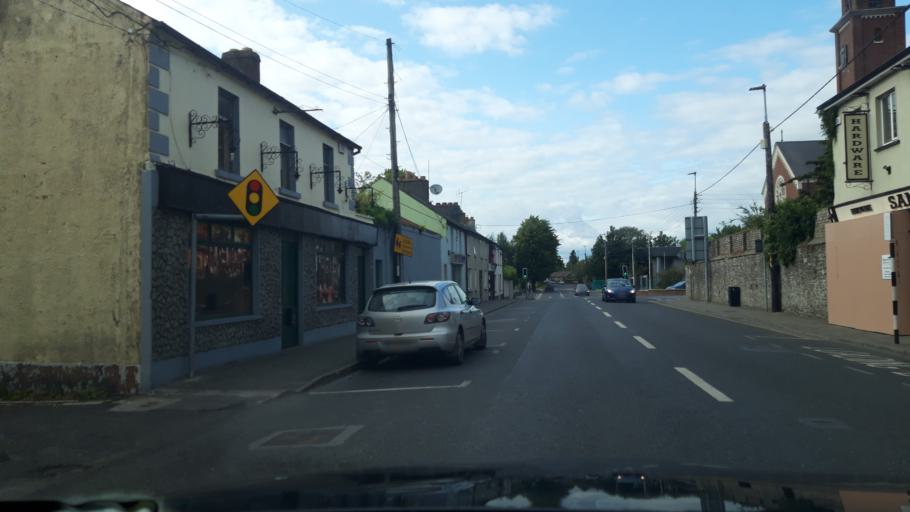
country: IE
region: Leinster
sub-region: Kildare
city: Athy
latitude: 52.9928
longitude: -6.9837
